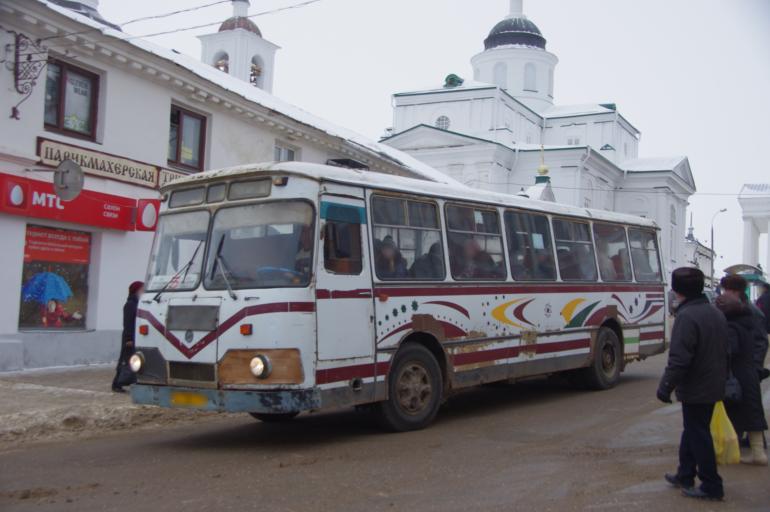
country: RU
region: Nizjnij Novgorod
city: Arzamas
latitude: 55.3861
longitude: 43.8158
